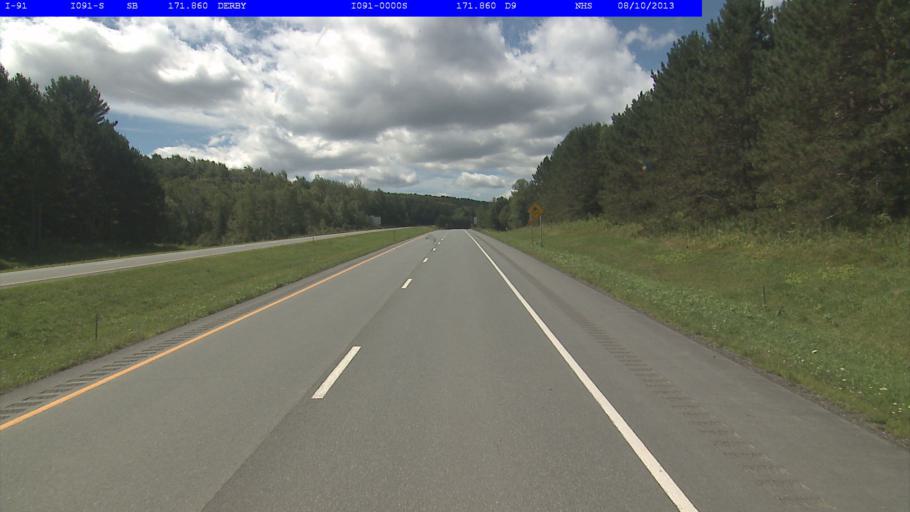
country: US
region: Vermont
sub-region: Orleans County
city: Newport
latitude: 44.9455
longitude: -72.1561
